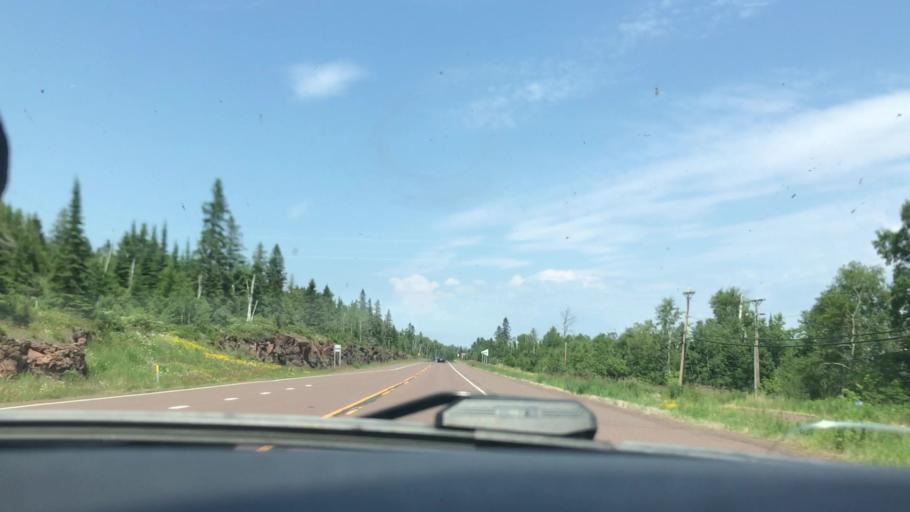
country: US
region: Minnesota
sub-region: Cook County
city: Grand Marais
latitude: 47.6146
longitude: -90.7588
